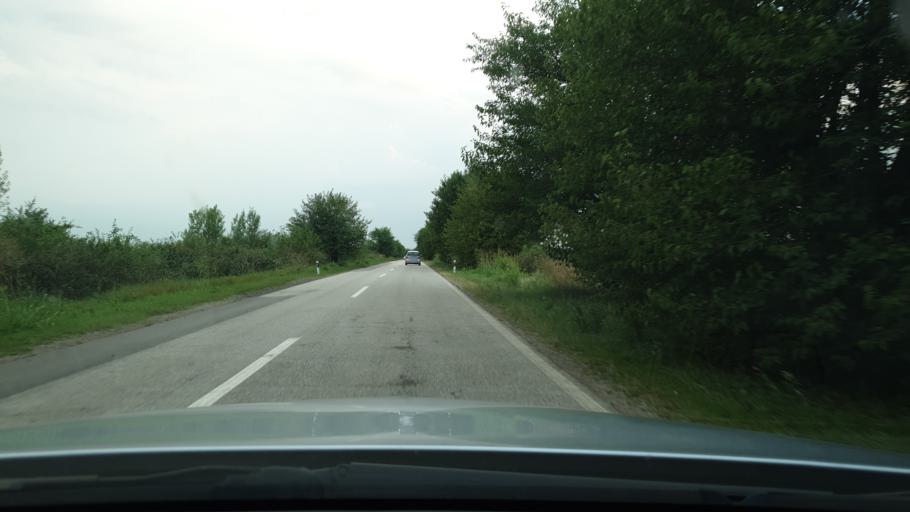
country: RS
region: Autonomna Pokrajina Vojvodina
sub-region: Juznobanatski Okrug
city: Vrsac
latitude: 45.0820
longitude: 21.2927
